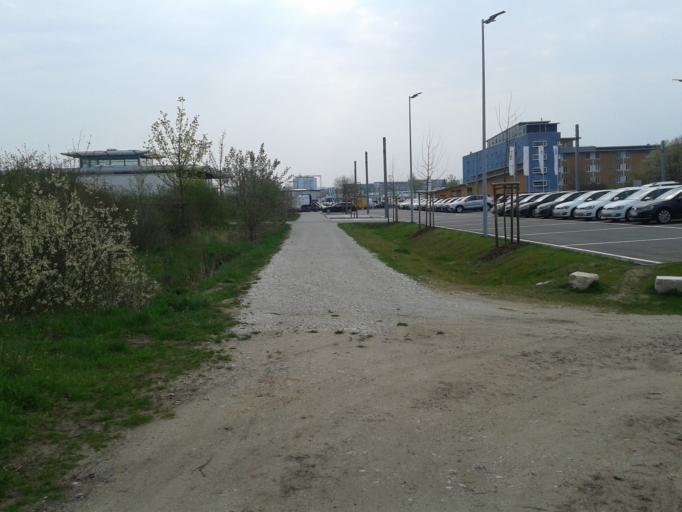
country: DE
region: Bavaria
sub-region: Upper Franconia
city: Bamberg
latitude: 49.9120
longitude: 10.8977
